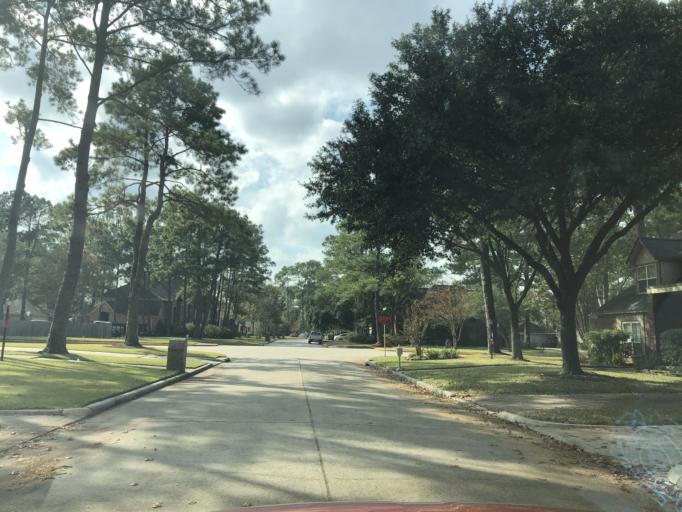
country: US
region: Texas
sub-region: Harris County
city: Tomball
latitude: 30.0204
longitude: -95.5454
